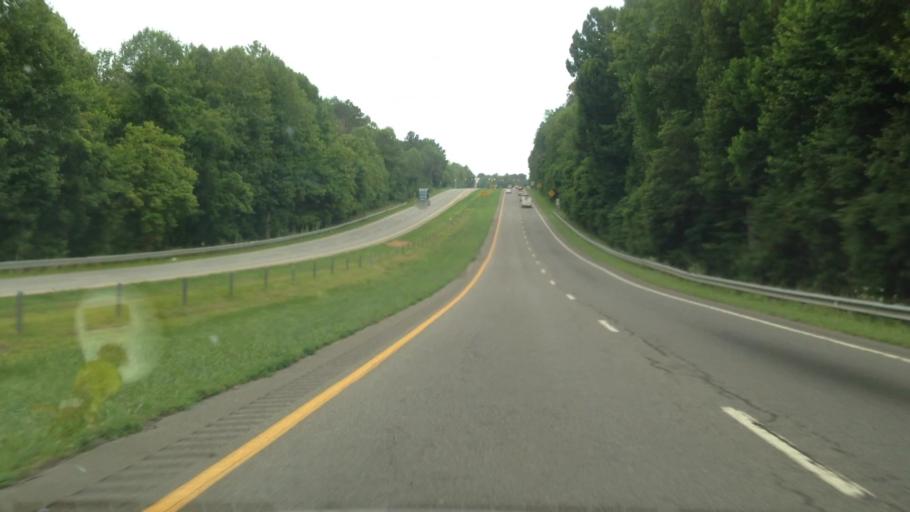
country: US
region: North Carolina
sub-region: Surry County
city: Flat Rock
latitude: 36.4664
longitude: -80.5677
